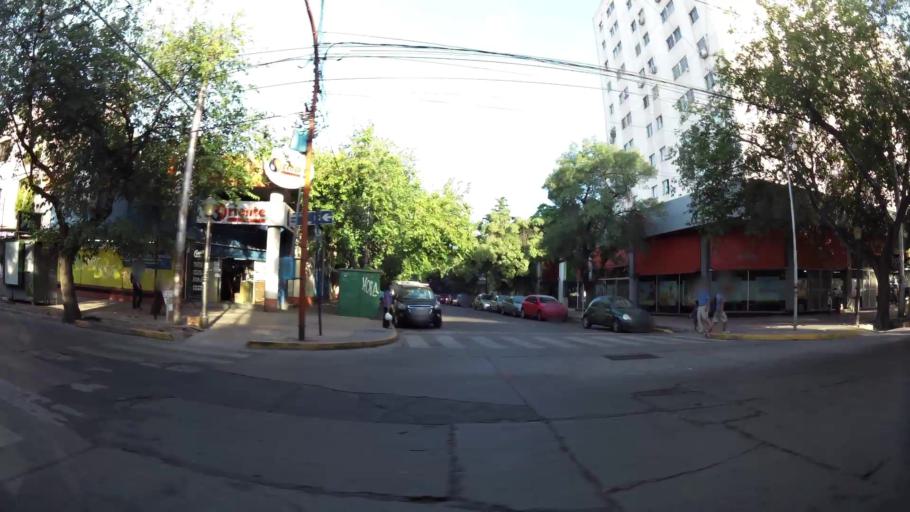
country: AR
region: Mendoza
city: Mendoza
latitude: -32.8973
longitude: -68.8386
